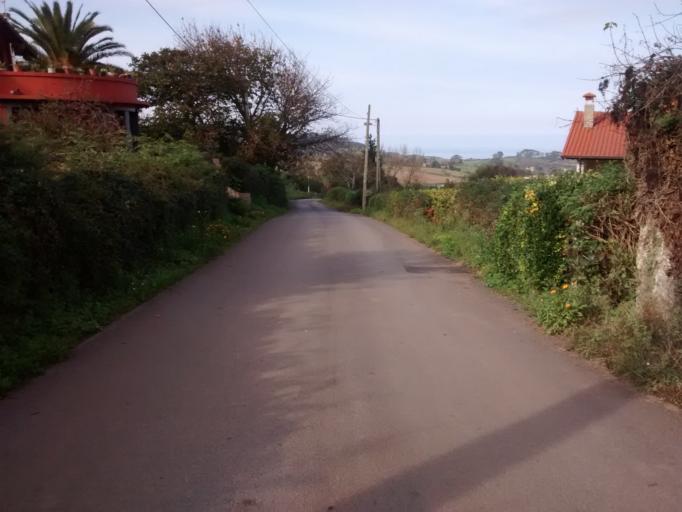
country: ES
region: Asturias
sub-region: Province of Asturias
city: Colunga
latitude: 43.4704
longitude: -5.2382
